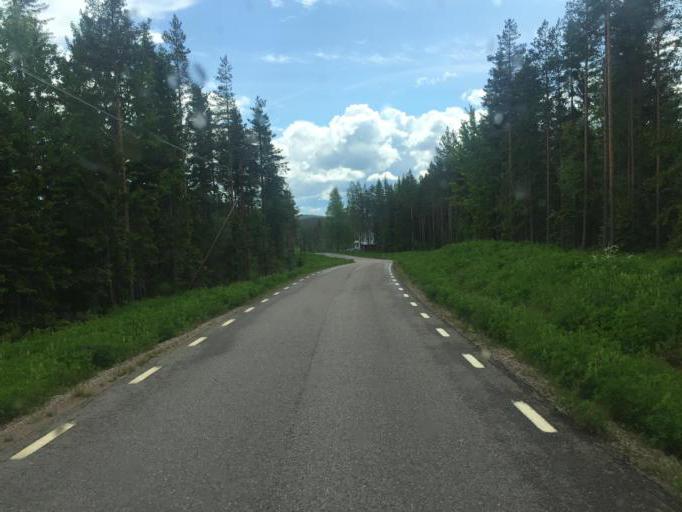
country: SE
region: Vaermland
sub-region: Hagfors Kommun
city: Hagfors
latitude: 60.2976
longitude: 13.8679
